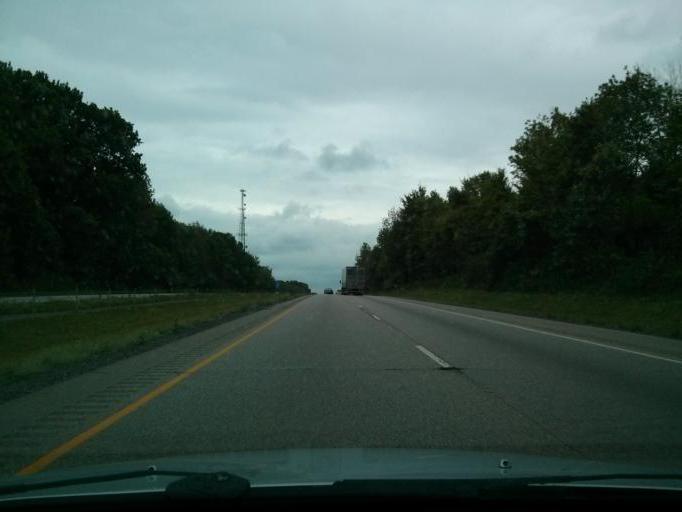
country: US
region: Ohio
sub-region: Portage County
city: Brimfield
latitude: 41.1087
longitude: -81.2946
